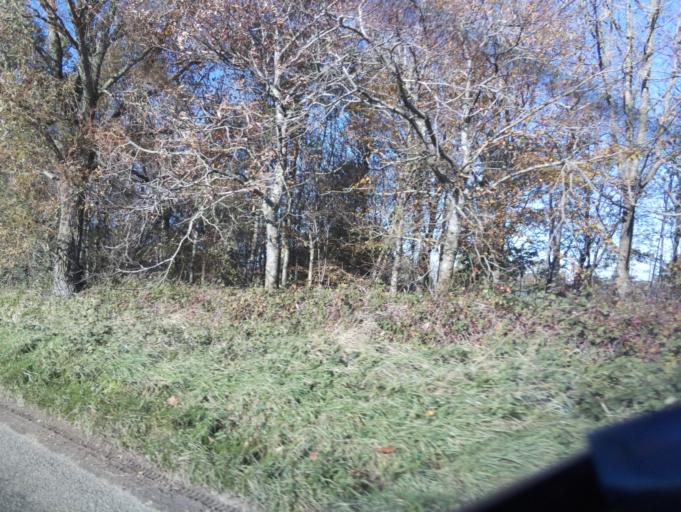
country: GB
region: England
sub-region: Somerset
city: Yeovil
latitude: 50.8969
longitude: -2.6098
